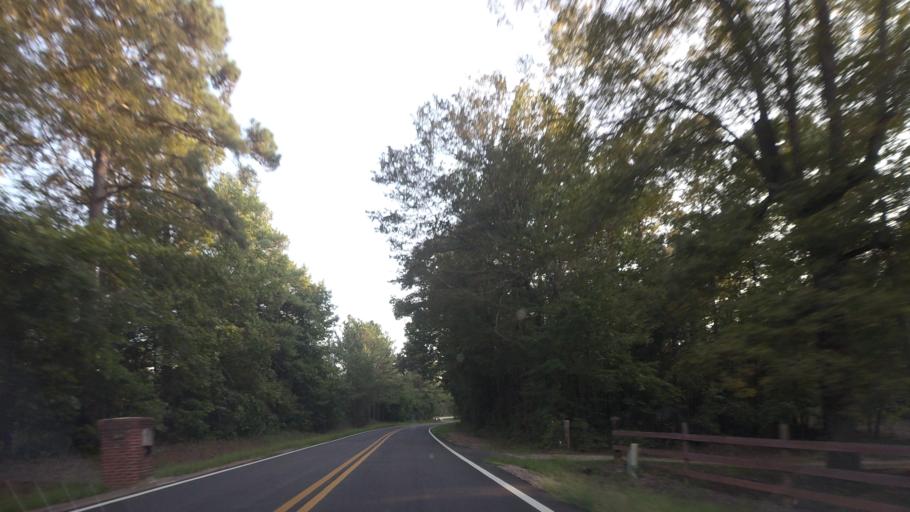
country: US
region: Georgia
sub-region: Bibb County
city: West Point
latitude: 32.8988
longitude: -83.8237
